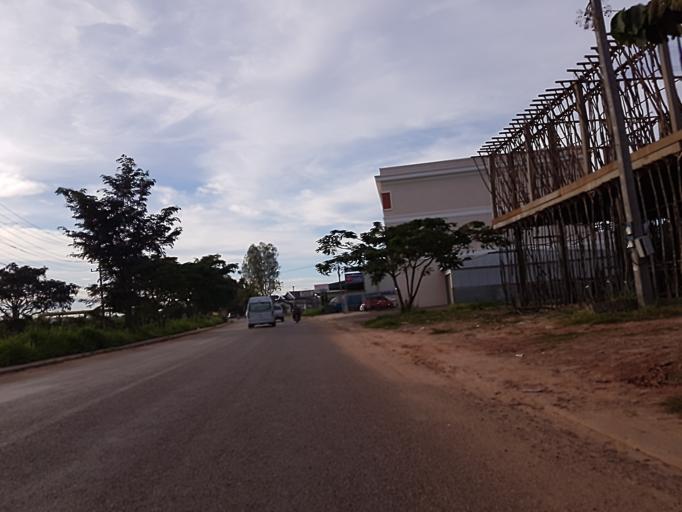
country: TH
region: Nong Khai
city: Si Chiang Mai
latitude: 18.0095
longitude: 102.5502
